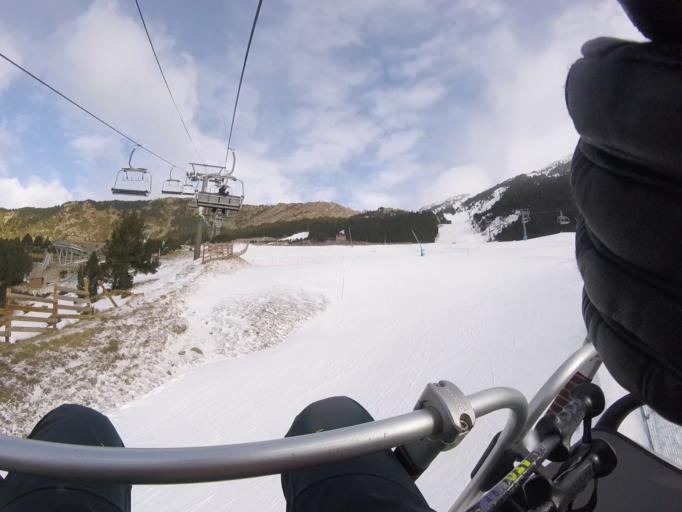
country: AD
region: Canillo
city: Canillo
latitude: 42.5539
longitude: 1.6135
